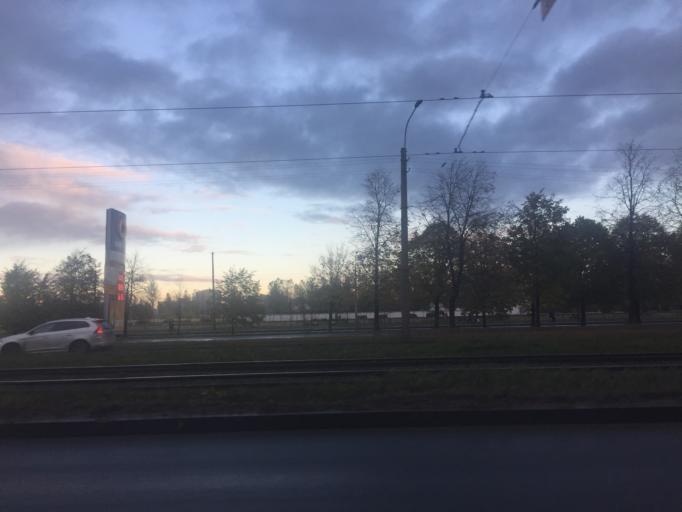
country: RU
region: St.-Petersburg
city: Obukhovo
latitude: 59.8881
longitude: 30.4640
